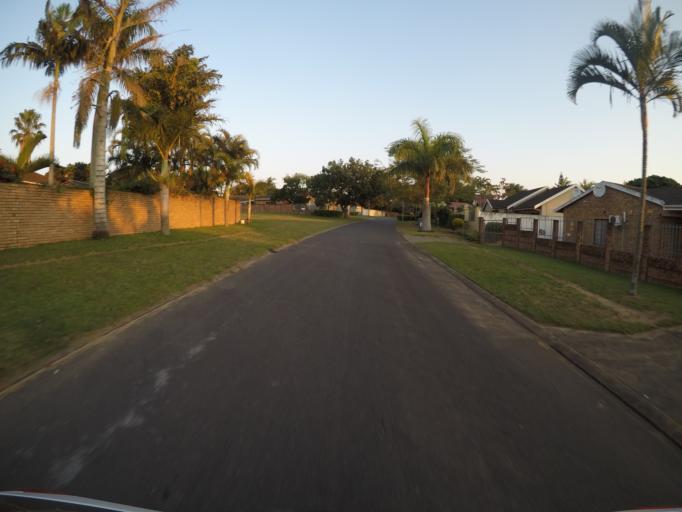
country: ZA
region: KwaZulu-Natal
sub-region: uThungulu District Municipality
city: Richards Bay
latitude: -28.7649
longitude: 32.1204
